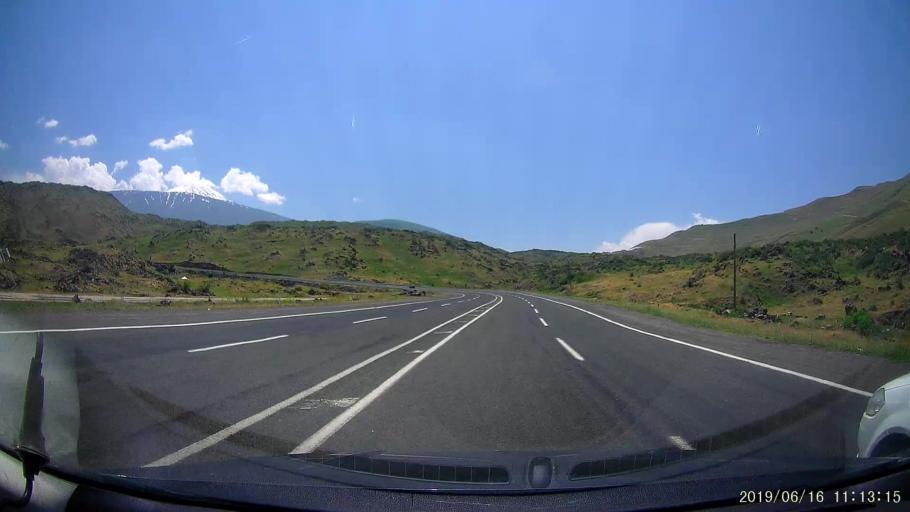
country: TR
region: Igdir
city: Igdir
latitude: 39.7864
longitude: 44.1354
